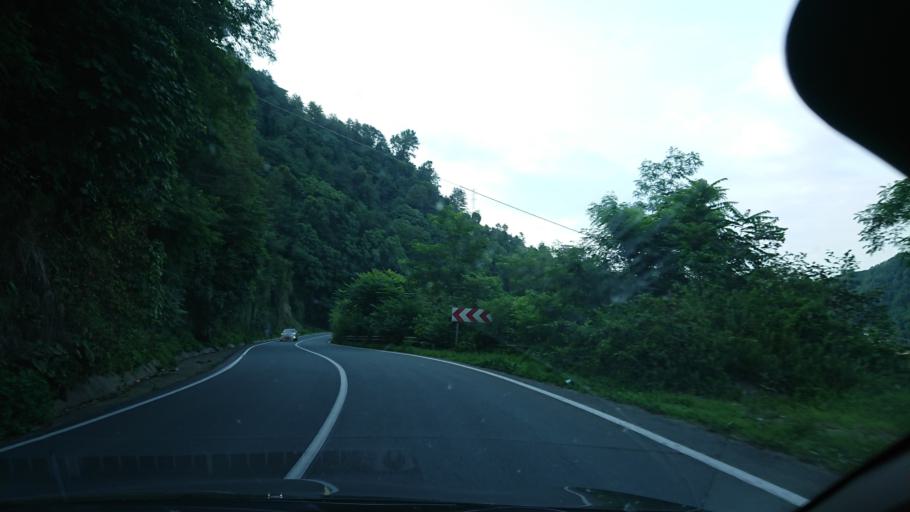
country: TR
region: Rize
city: Cayeli
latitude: 41.0743
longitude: 40.7116
